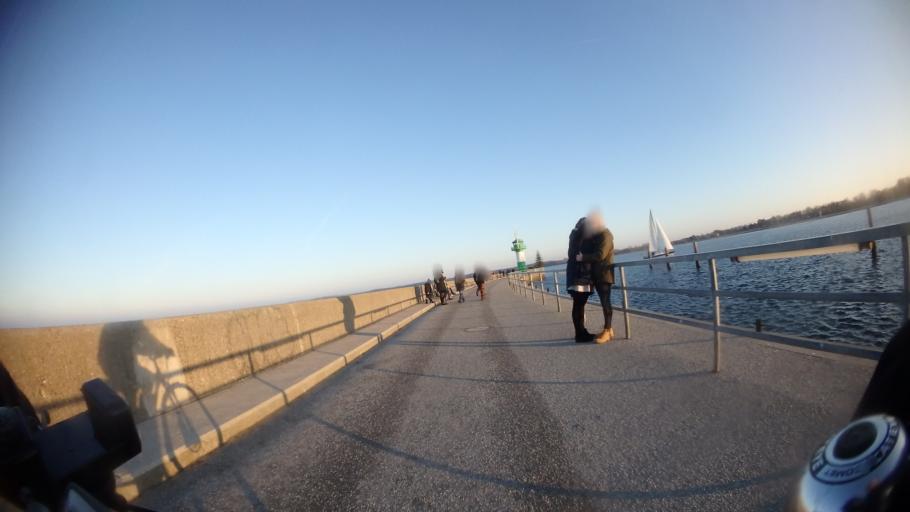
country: DE
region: Schleswig-Holstein
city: Travemuende
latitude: 53.9622
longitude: 10.8874
